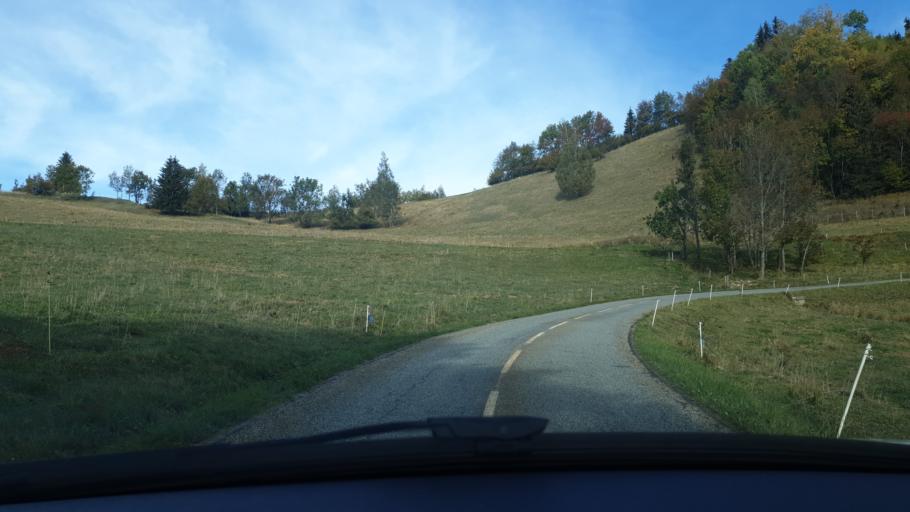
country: FR
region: Rhone-Alpes
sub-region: Departement de la Savoie
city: Aiton
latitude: 45.5029
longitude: 6.2217
